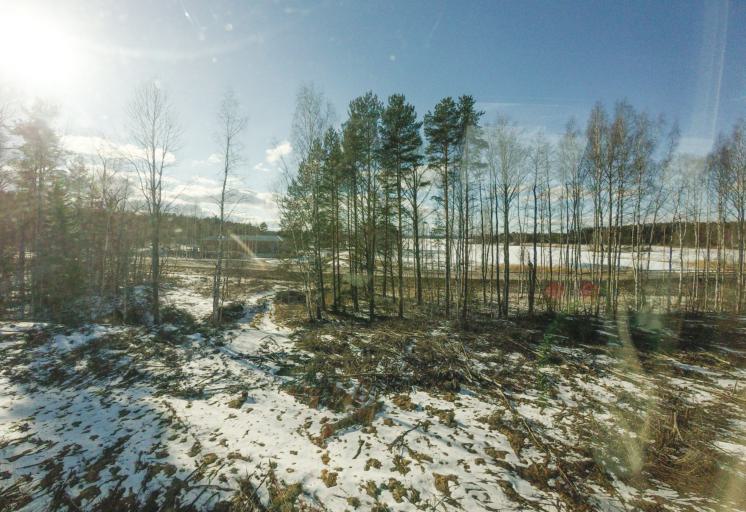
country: FI
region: South Karelia
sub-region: Imatra
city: Parikkala
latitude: 61.4940
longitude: 29.4862
